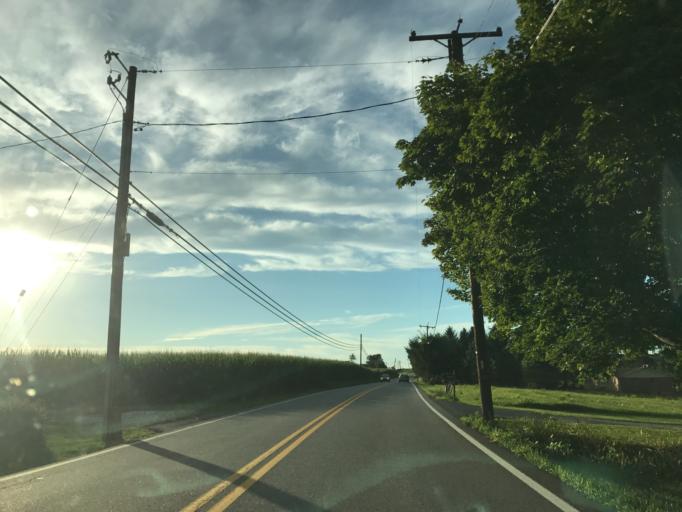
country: US
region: Pennsylvania
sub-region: York County
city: New Freedom
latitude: 39.6818
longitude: -76.7307
